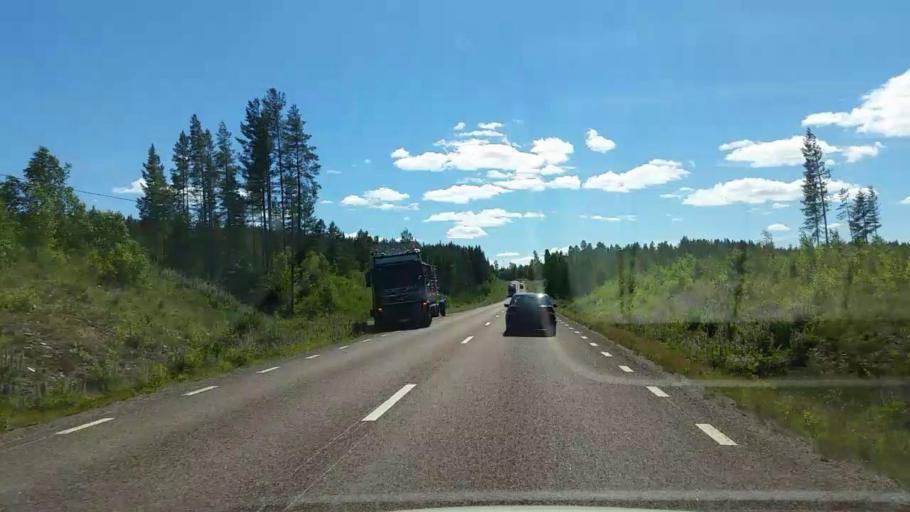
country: SE
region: Gaevleborg
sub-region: Ovanakers Kommun
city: Edsbyn
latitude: 61.2624
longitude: 15.8875
